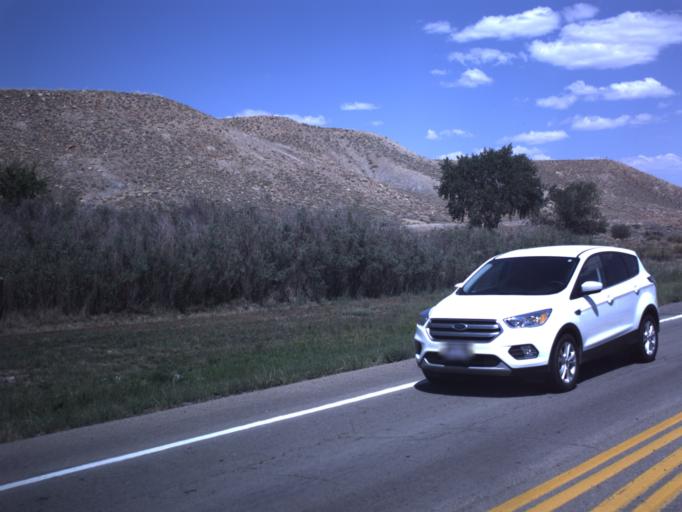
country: US
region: Utah
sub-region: Emery County
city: Castle Dale
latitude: 39.2118
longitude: -111.0051
